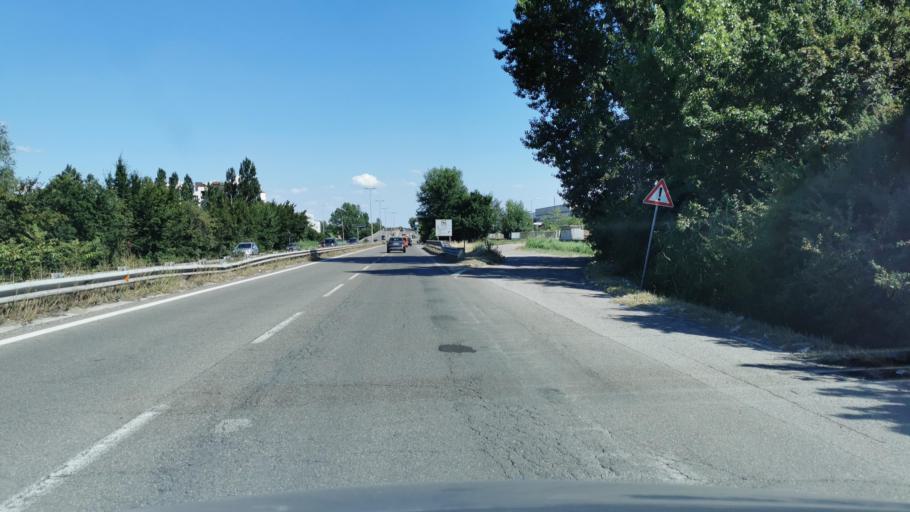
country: IT
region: Emilia-Romagna
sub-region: Provincia di Modena
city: Modena
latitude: 44.6668
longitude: 10.9333
